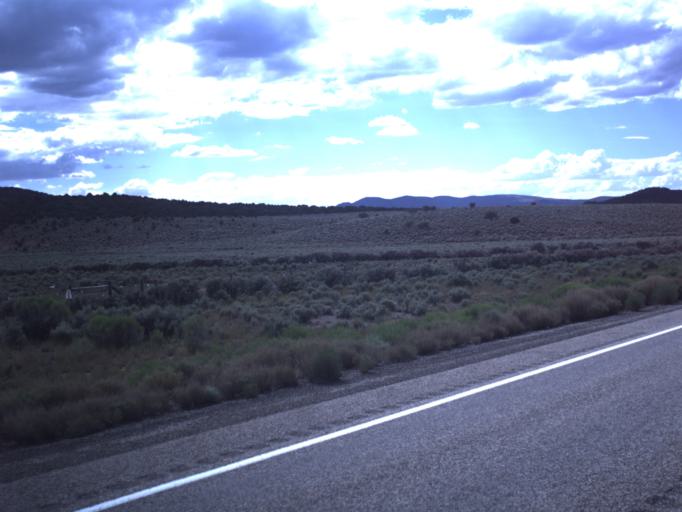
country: US
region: Utah
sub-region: Beaver County
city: Beaver
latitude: 38.0600
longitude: -112.5886
